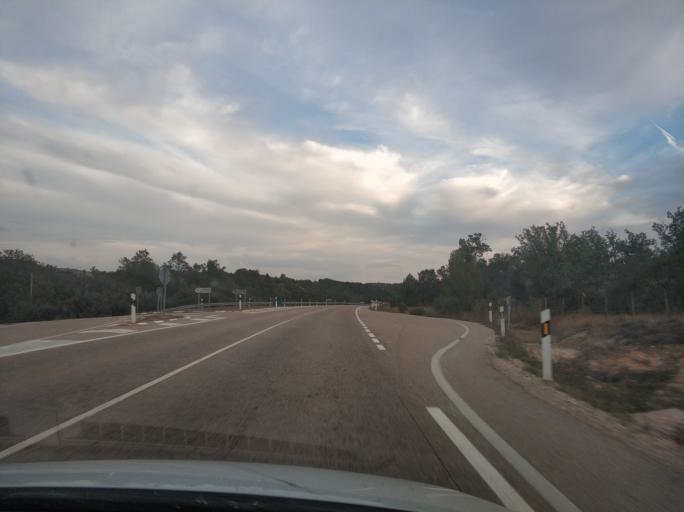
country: ES
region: Castille and Leon
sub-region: Provincia de Burgos
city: Pinilla de los Barruecos
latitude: 41.9267
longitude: -3.2804
